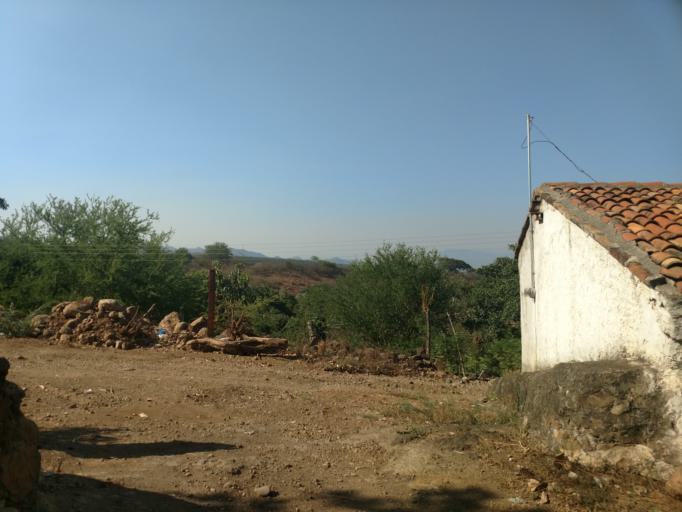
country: MX
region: Nayarit
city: Santa Maria del Oro
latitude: 21.4677
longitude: -104.6542
